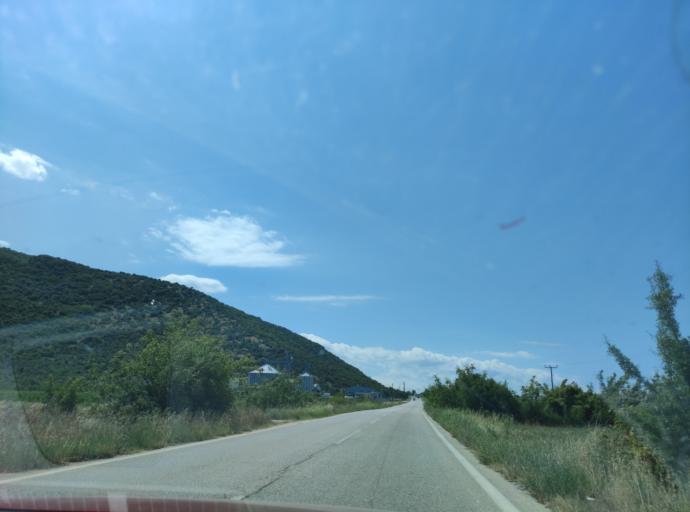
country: GR
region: East Macedonia and Thrace
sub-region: Nomos Kavalas
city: Palaiochori
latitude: 40.9702
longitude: 24.1691
